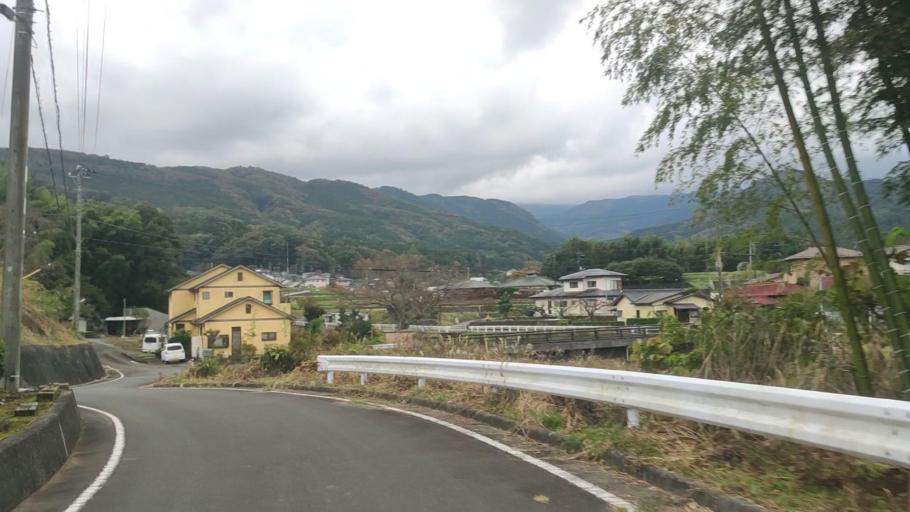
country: JP
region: Shizuoka
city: Ito
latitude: 34.9348
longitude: 139.0002
